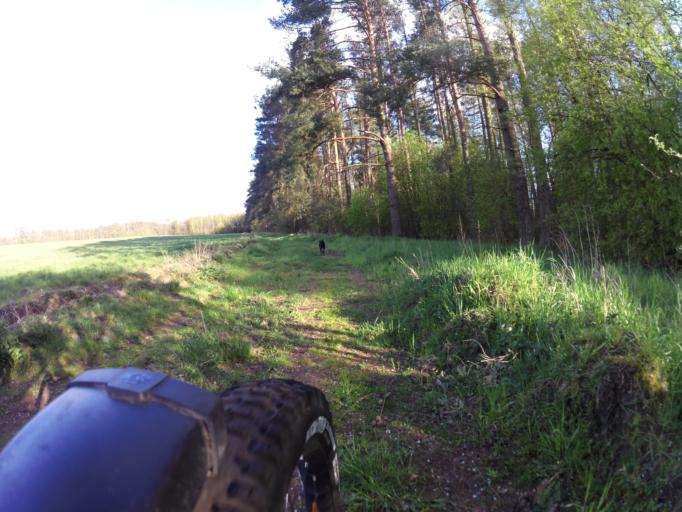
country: PL
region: West Pomeranian Voivodeship
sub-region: Powiat gryficki
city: Ploty
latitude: 53.7649
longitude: 15.2613
